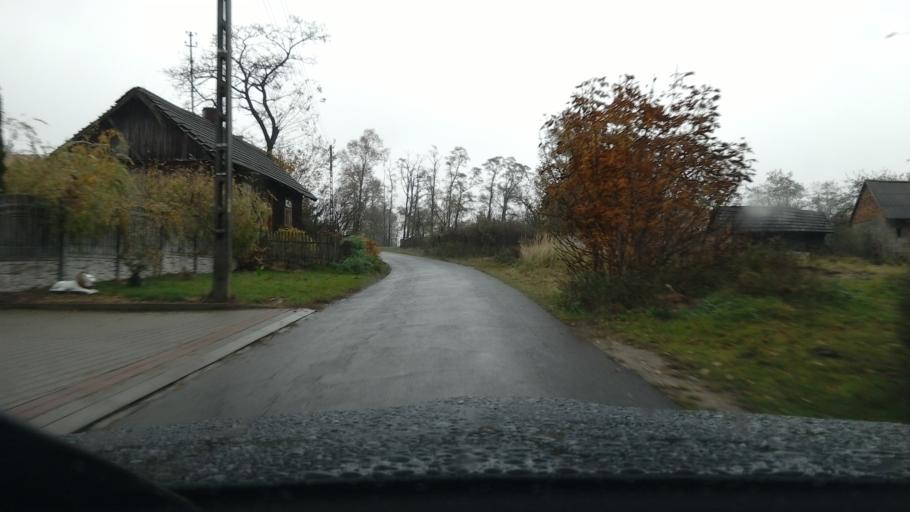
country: PL
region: Lodz Voivodeship
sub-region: Powiat skierniewicki
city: Godzianow
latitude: 51.9006
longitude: 20.0570
